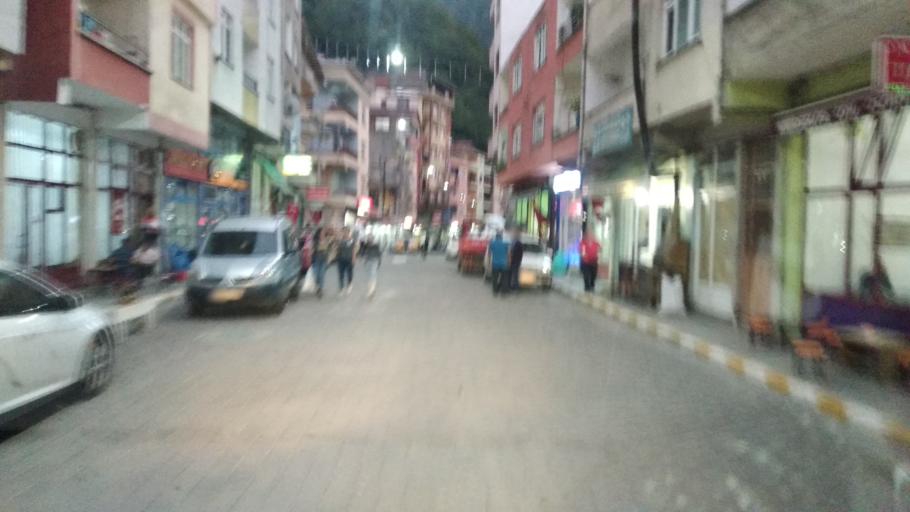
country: TR
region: Giresun
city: Dogankent
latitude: 40.8070
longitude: 38.9178
